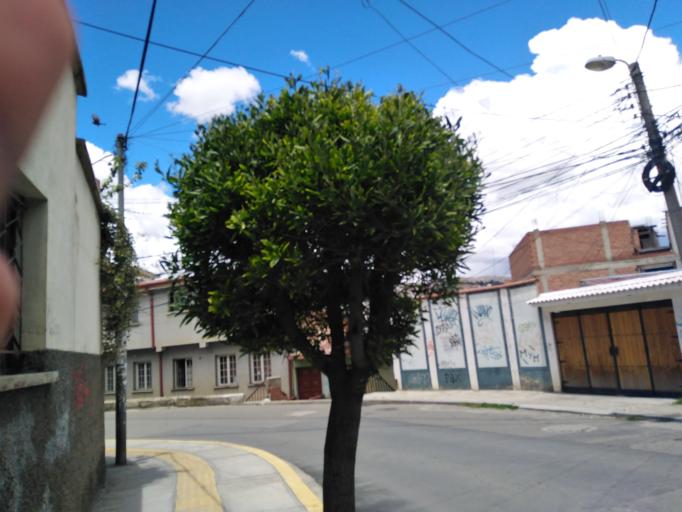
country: BO
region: La Paz
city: La Paz
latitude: -16.5070
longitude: -68.1366
